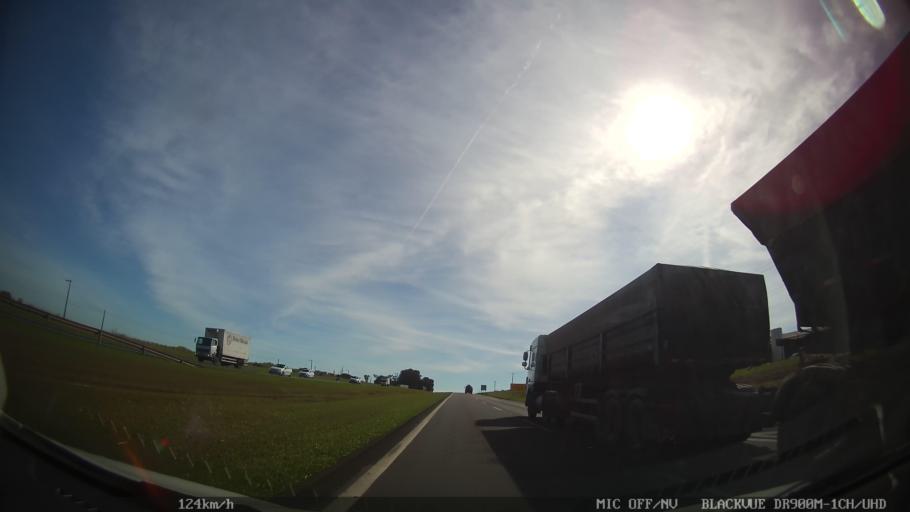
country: BR
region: Sao Paulo
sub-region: Cordeiropolis
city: Cordeiropolis
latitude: -22.4667
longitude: -47.3990
